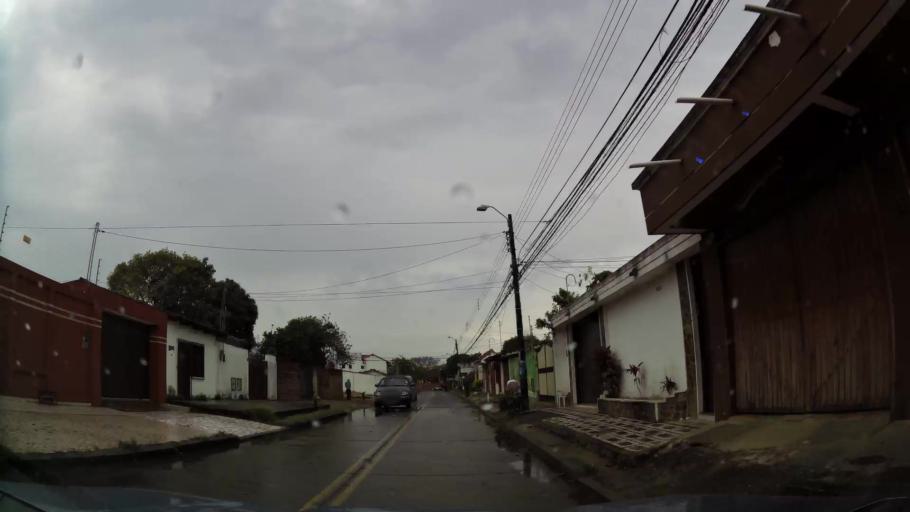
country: BO
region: Santa Cruz
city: Santa Cruz de la Sierra
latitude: -17.7705
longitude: -63.1527
